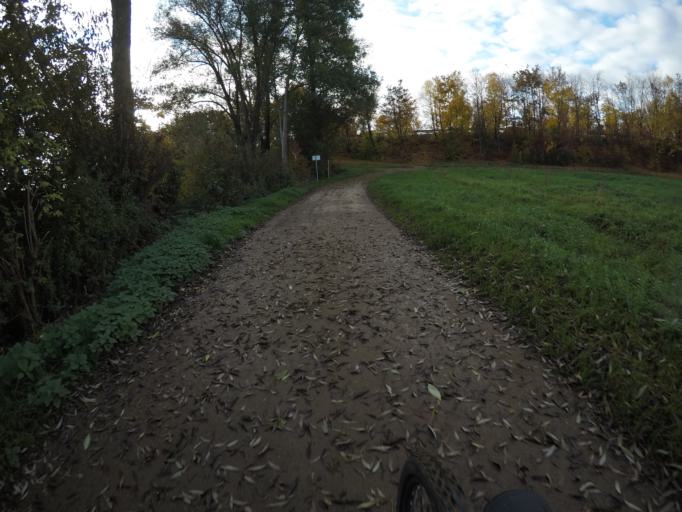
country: DE
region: Baden-Wuerttemberg
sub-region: Regierungsbezirk Stuttgart
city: Leinfelden-Echterdingen
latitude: 48.6758
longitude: 9.1892
